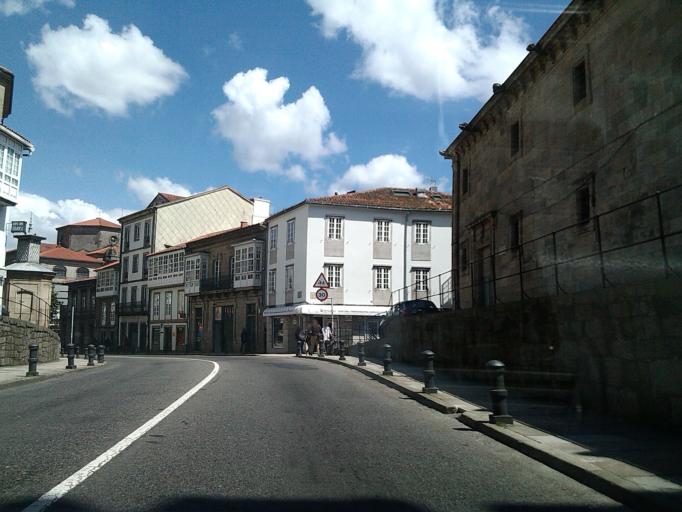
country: ES
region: Galicia
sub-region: Provincia da Coruna
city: Santiago de Compostela
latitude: 42.8778
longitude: -8.5420
